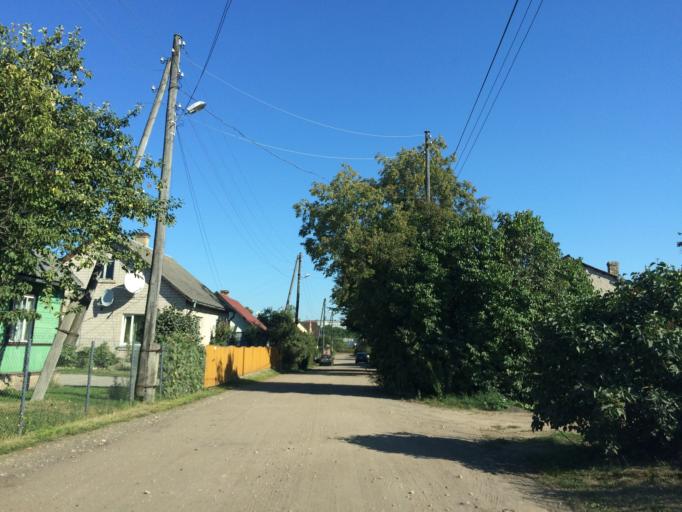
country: LV
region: Rezekne
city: Rezekne
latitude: 56.5006
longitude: 27.3440
